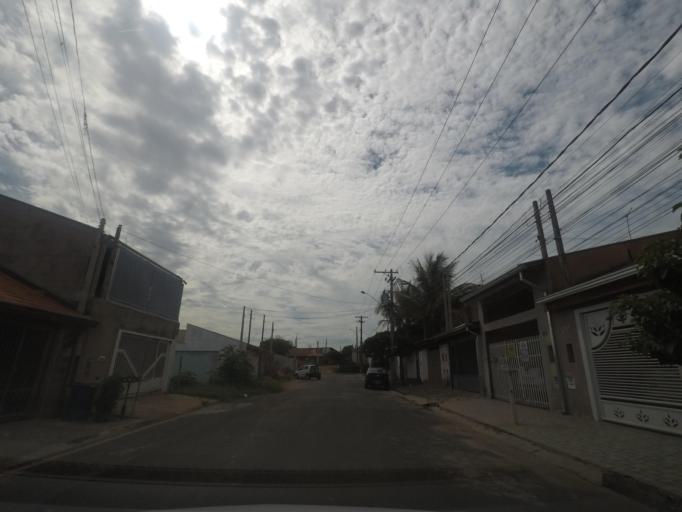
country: BR
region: Sao Paulo
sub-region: Sumare
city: Sumare
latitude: -22.8104
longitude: -47.2705
